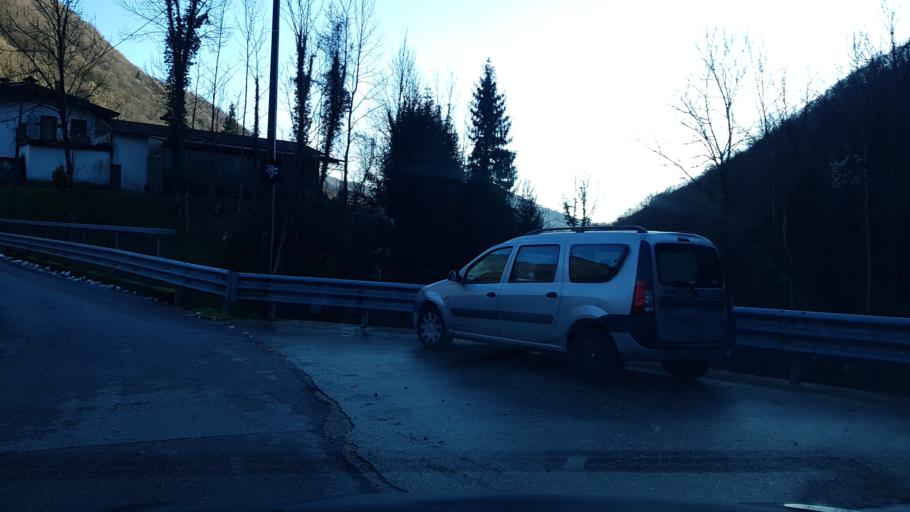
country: IT
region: Friuli Venezia Giulia
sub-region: Provincia di Udine
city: Savogna
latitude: 46.1774
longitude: 13.5367
